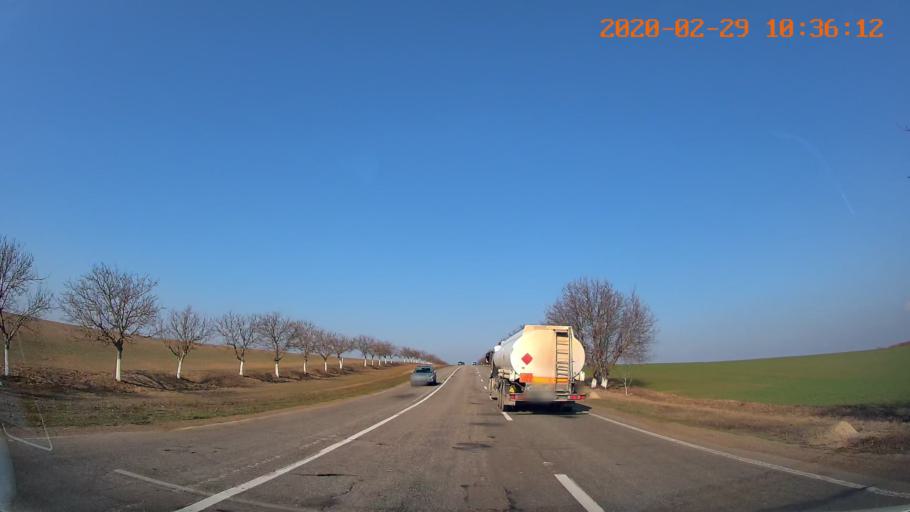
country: MD
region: Anenii Noi
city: Varnita
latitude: 46.9929
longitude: 29.5093
